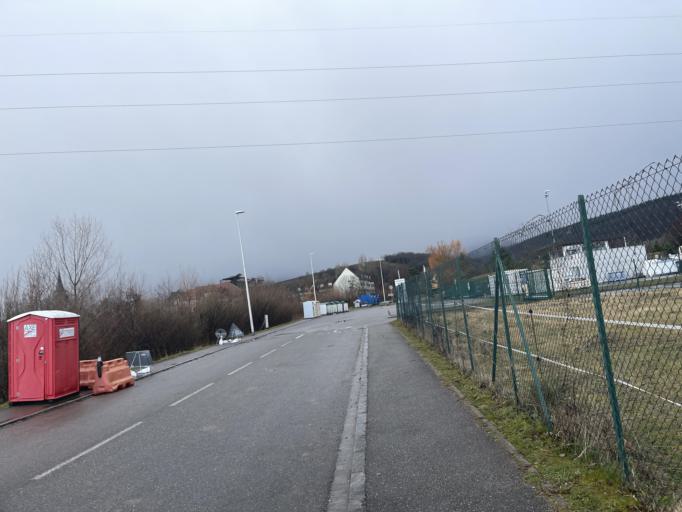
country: FR
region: Alsace
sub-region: Departement du Haut-Rhin
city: Soultz-Haut-Rhin
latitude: 47.8905
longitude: 7.2345
